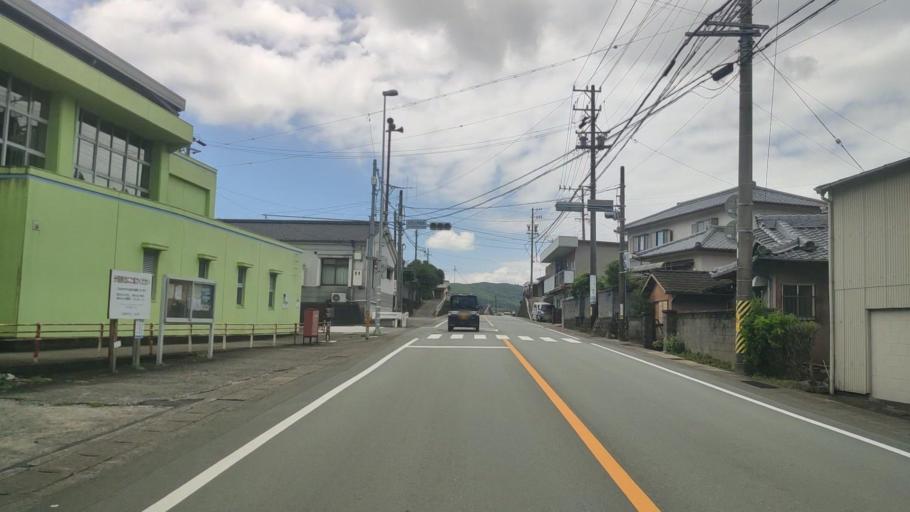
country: JP
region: Mie
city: Toba
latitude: 34.4446
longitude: 136.8441
